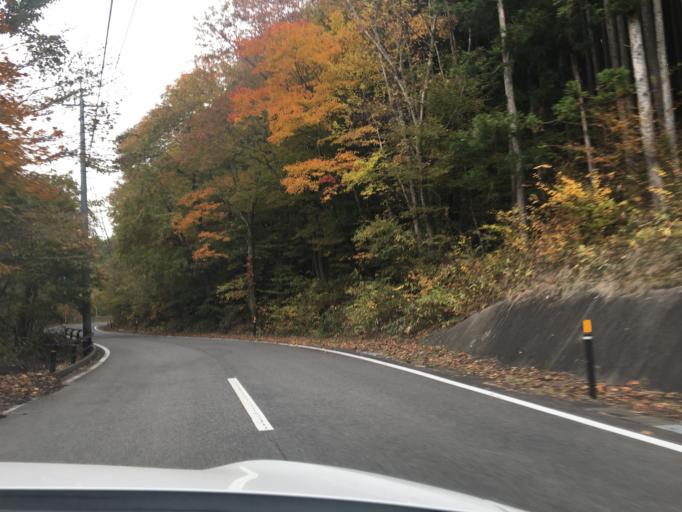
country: JP
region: Fukushima
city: Iwaki
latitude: 37.2026
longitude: 140.6981
